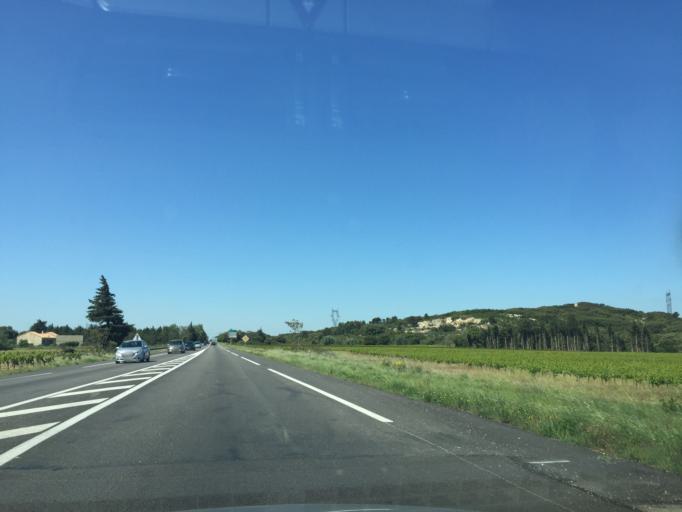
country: FR
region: Languedoc-Roussillon
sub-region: Departement du Gard
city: Saze
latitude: 43.9502
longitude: 4.6363
